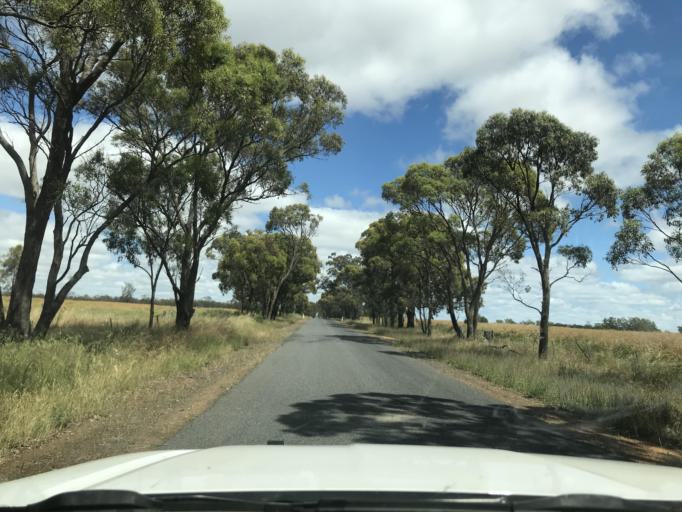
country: AU
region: South Australia
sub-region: Naracoorte and Lucindale
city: Naracoorte
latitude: -36.6835
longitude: 141.3140
